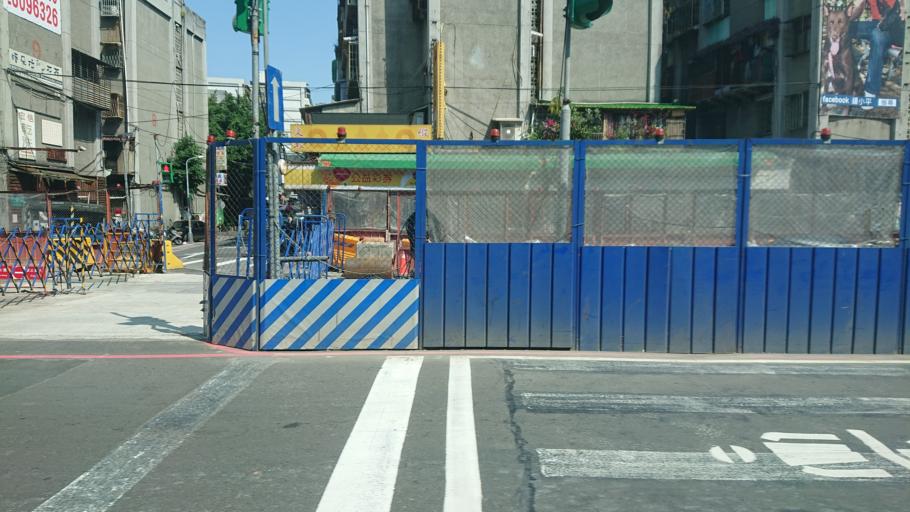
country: TW
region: Taipei
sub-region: Taipei
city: Banqiao
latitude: 25.0279
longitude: 121.5004
